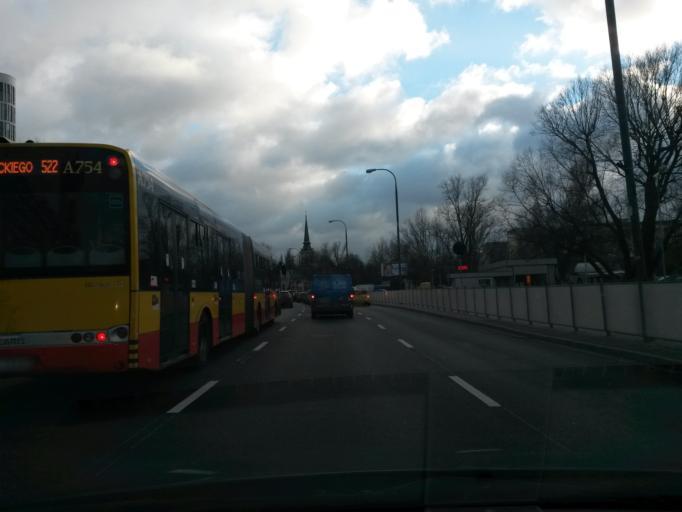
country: PL
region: Masovian Voivodeship
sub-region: Warszawa
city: Srodmiescie
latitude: 52.2139
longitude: 21.0168
